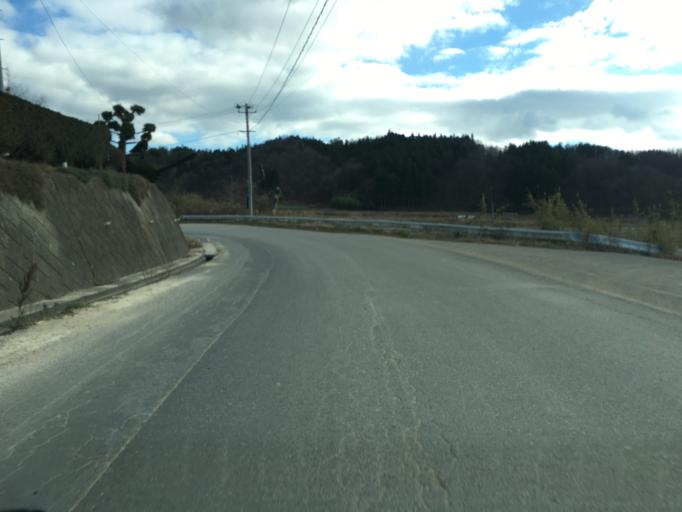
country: JP
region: Fukushima
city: Ishikawa
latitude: 37.2161
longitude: 140.5575
